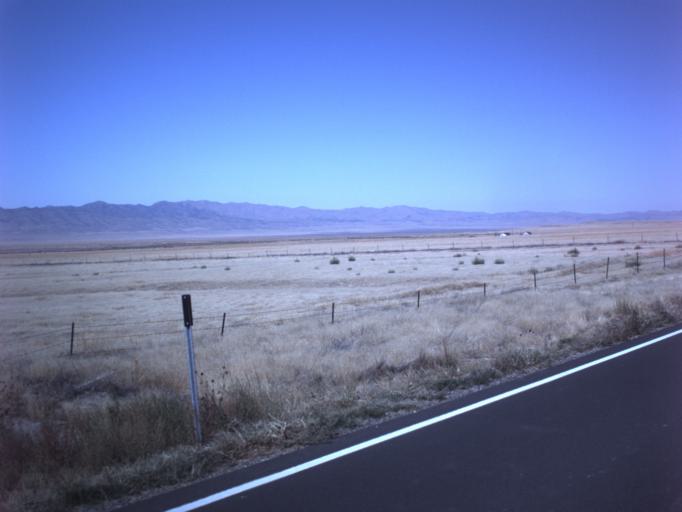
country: US
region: Utah
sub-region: Tooele County
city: Grantsville
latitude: 40.3907
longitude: -112.7474
